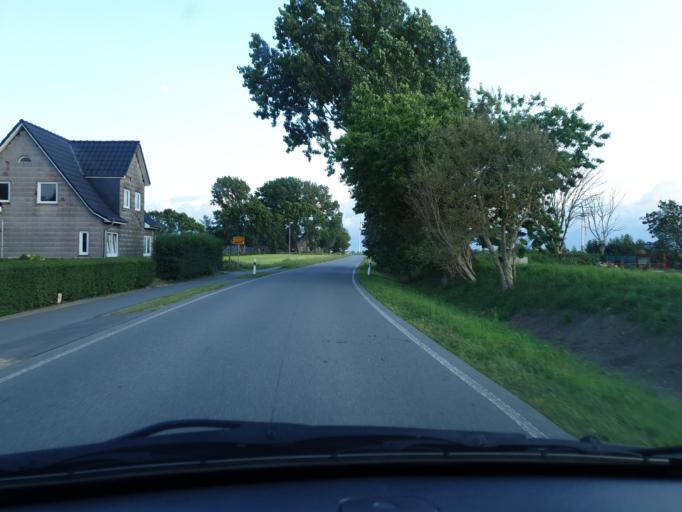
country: DE
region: Schleswig-Holstein
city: Diekhusen-Fahrstedt
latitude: 53.9422
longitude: 9.0129
